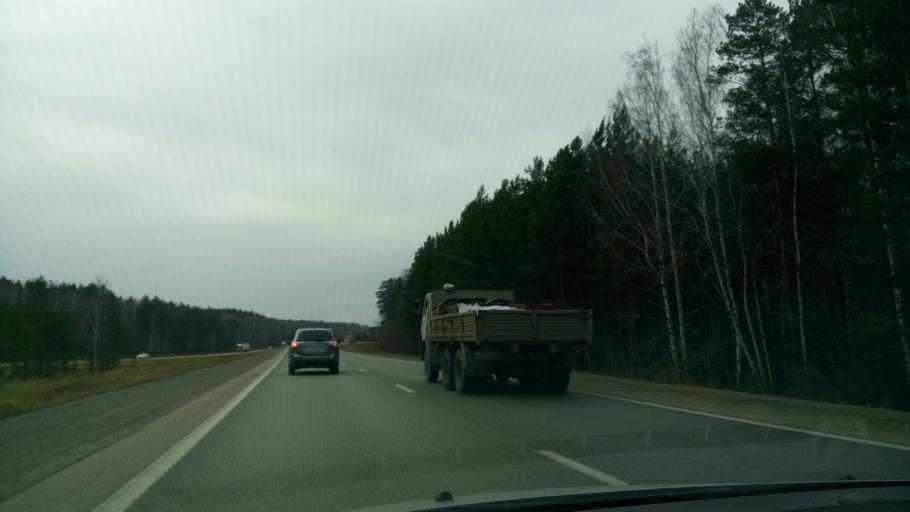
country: RU
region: Sverdlovsk
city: Verkhneye Dubrovo
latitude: 56.7343
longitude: 61.0787
